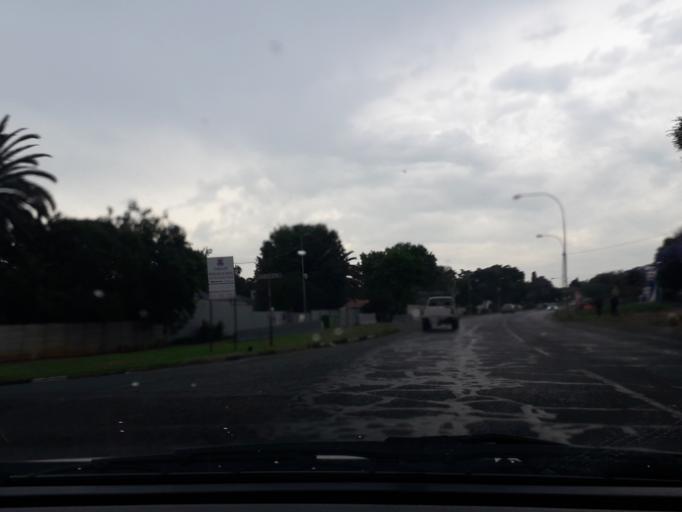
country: ZA
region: Gauteng
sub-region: City of Johannesburg Metropolitan Municipality
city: Johannesburg
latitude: -26.1478
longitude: 28.1022
